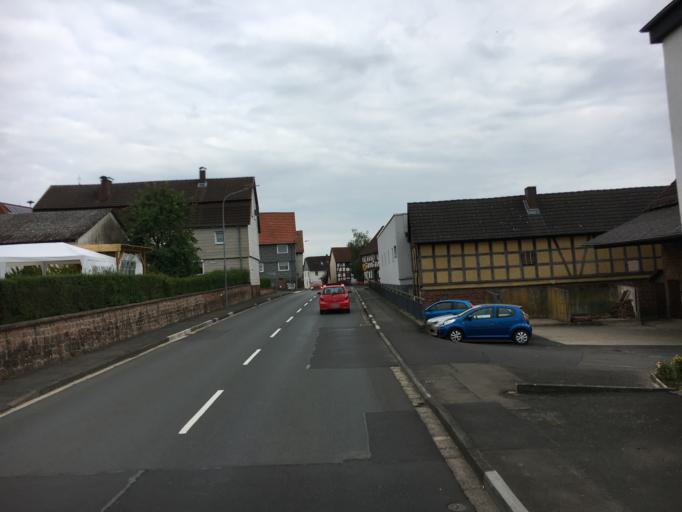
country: DE
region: Hesse
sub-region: Regierungsbezirk Giessen
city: Colbe
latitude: 50.8453
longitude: 8.8624
